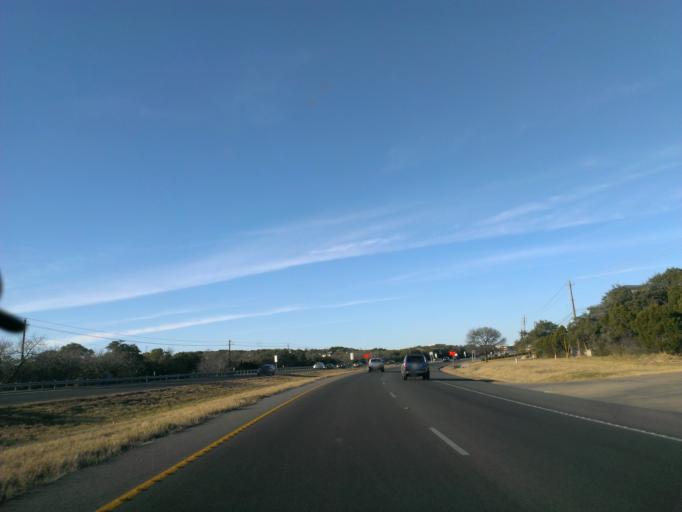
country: US
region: Texas
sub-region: Travis County
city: Rollingwood
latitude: 30.2659
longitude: -97.8180
